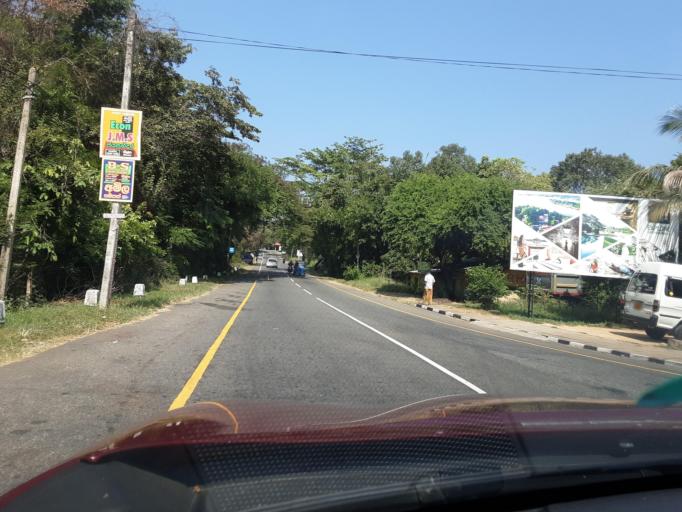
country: LK
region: Uva
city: Badulla
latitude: 7.2833
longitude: 81.0431
